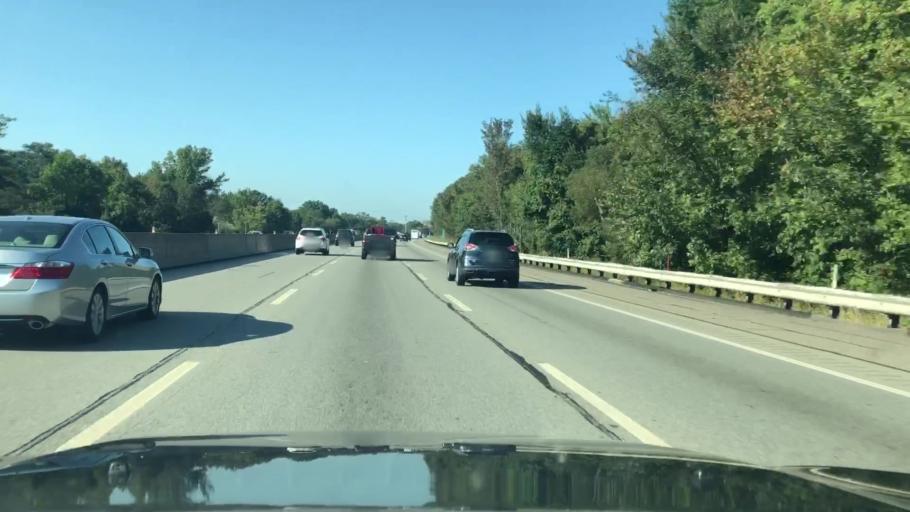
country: US
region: Pennsylvania
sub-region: Montgomery County
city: Dresher
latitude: 40.1426
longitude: -75.1569
